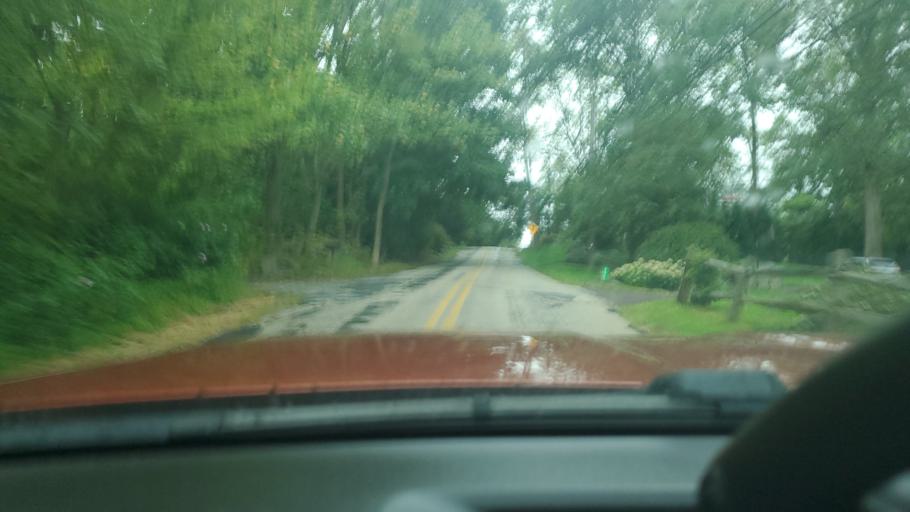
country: US
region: Pennsylvania
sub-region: Montgomery County
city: Woxall
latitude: 40.3149
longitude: -75.4941
